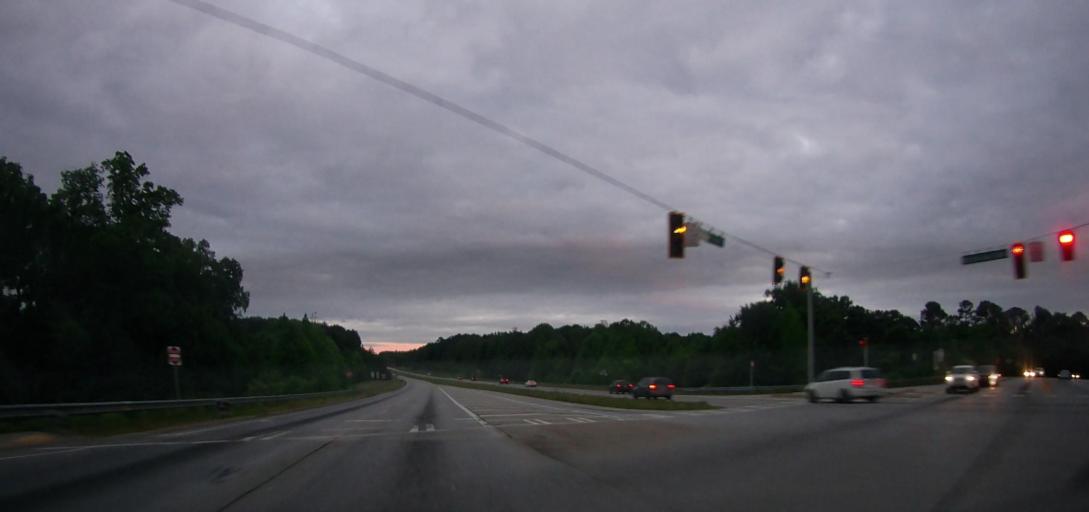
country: US
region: Georgia
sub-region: Jackson County
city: Jefferson
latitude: 34.1040
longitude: -83.5934
